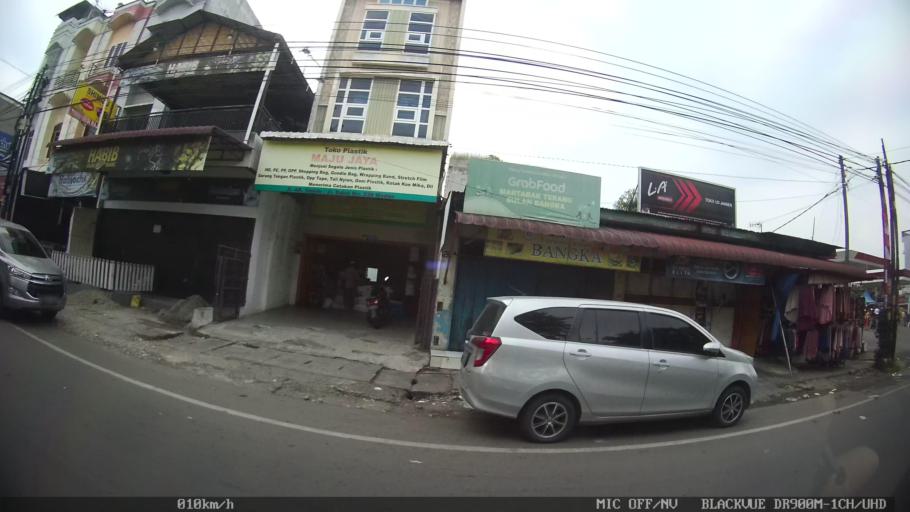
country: ID
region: North Sumatra
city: Medan
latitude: 3.5724
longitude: 98.7030
